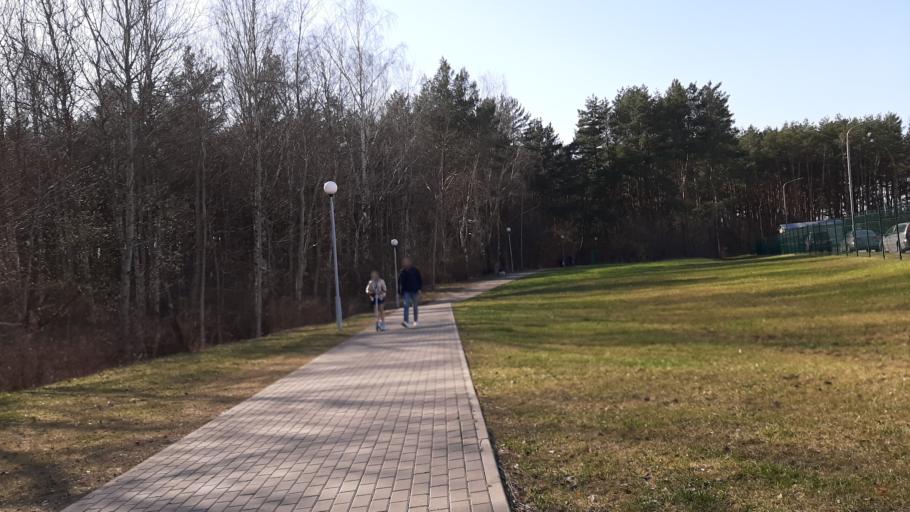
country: BY
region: Minsk
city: Bal'shavik
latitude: 53.9578
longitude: 27.5934
